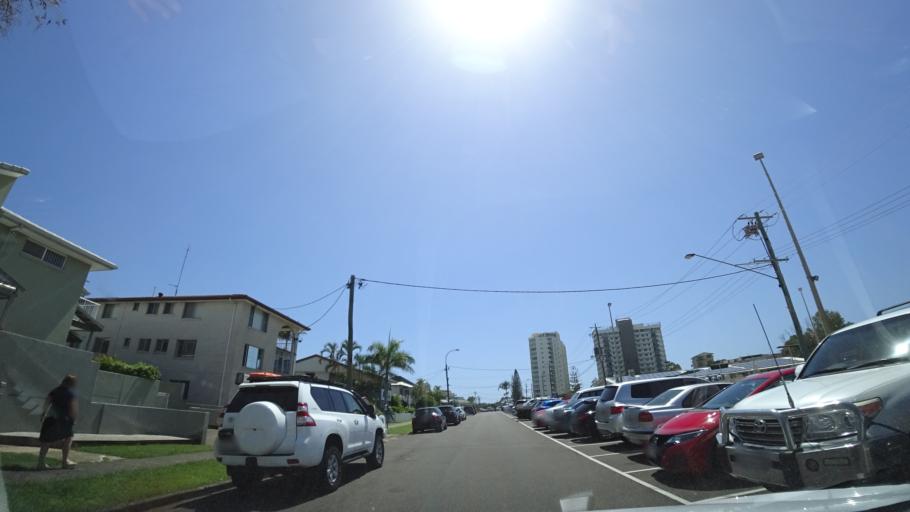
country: AU
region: Queensland
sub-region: Sunshine Coast
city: Mooloolaba
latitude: -26.6558
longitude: 153.1001
